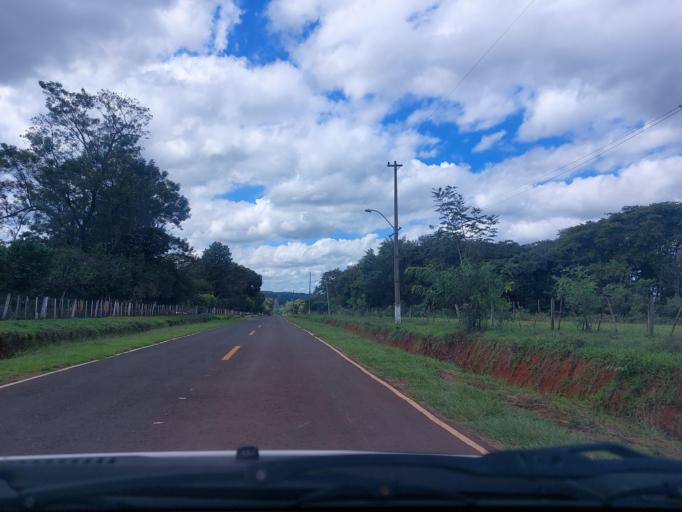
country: PY
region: San Pedro
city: Guayaybi
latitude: -24.5316
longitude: -56.5411
